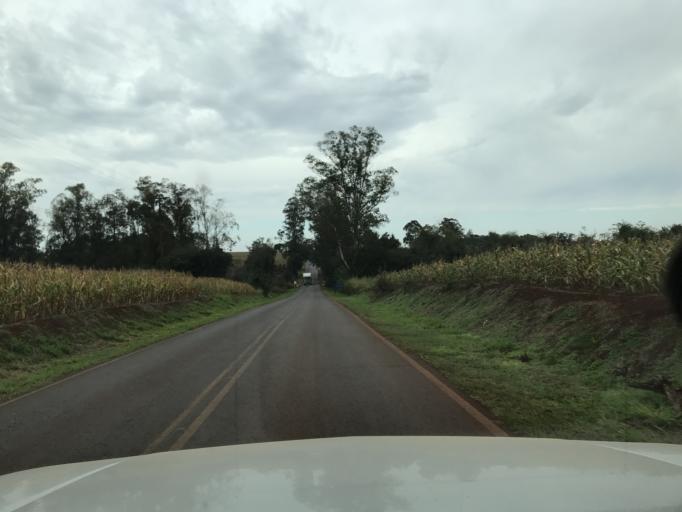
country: BR
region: Parana
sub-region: Marechal Candido Rondon
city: Marechal Candido Rondon
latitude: -24.4487
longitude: -53.9234
